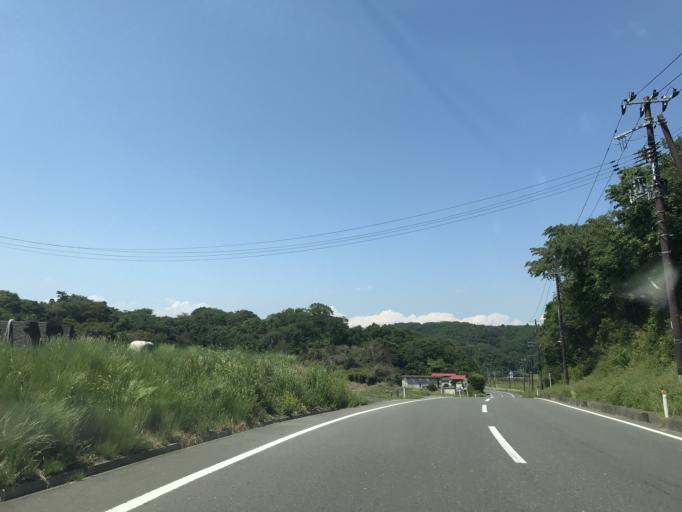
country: JP
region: Miyagi
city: Matsushima
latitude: 38.3269
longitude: 141.1550
